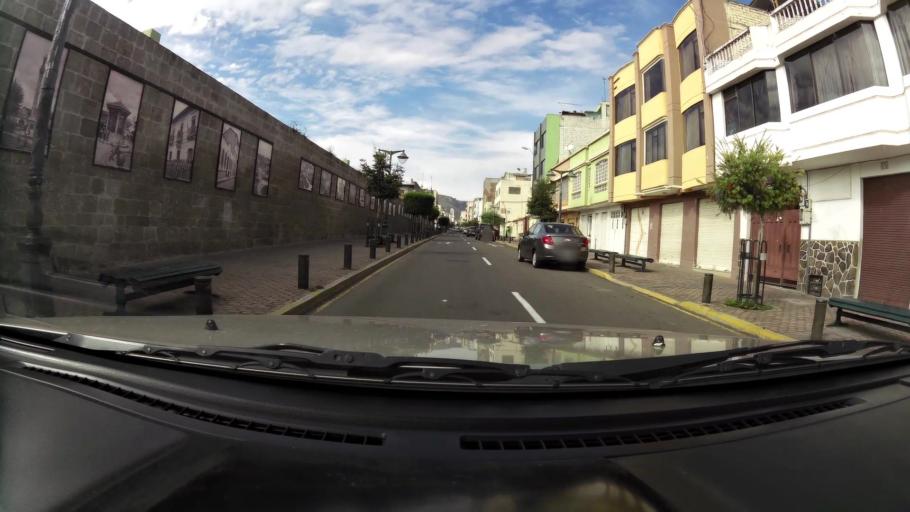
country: EC
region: Tungurahua
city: Ambato
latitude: -1.2357
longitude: -78.6232
